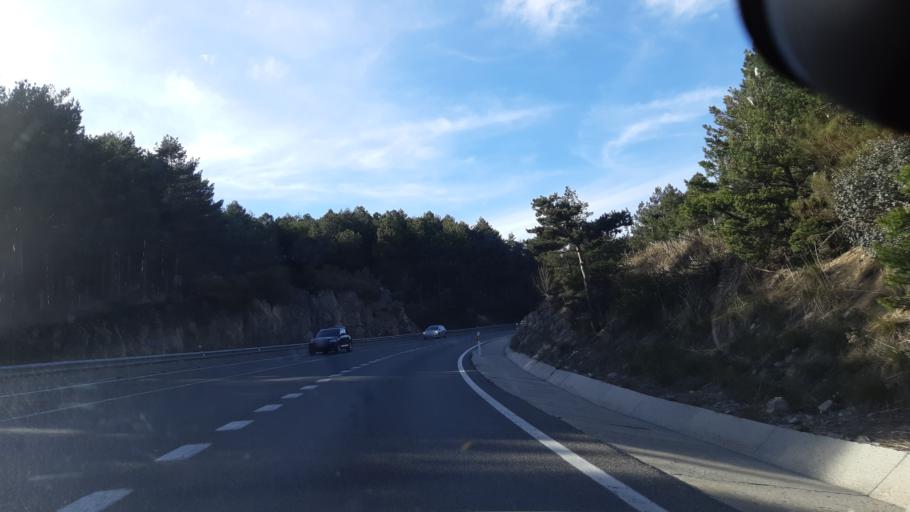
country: ES
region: Madrid
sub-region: Provincia de Madrid
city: Guadarrama
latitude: 40.7068
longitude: -4.1319
